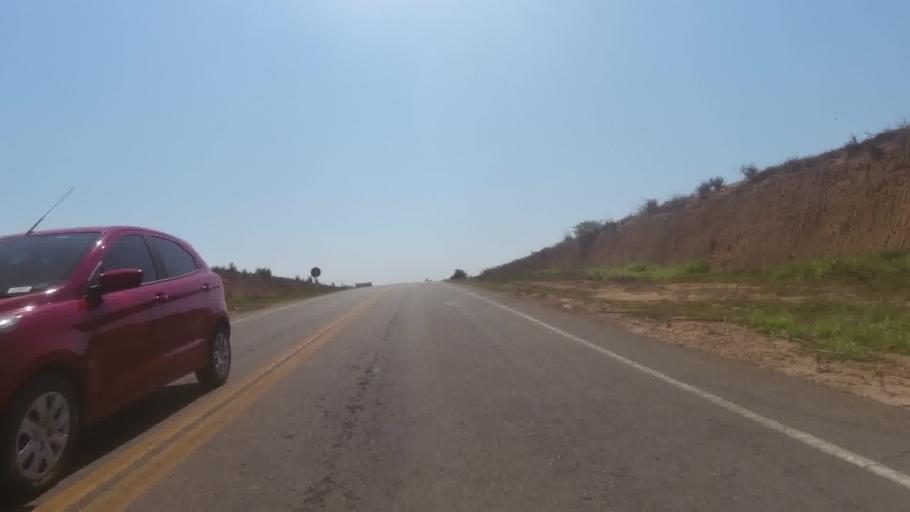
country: BR
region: Espirito Santo
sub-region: Marataizes
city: Marataizes
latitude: -21.0574
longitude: -40.8487
